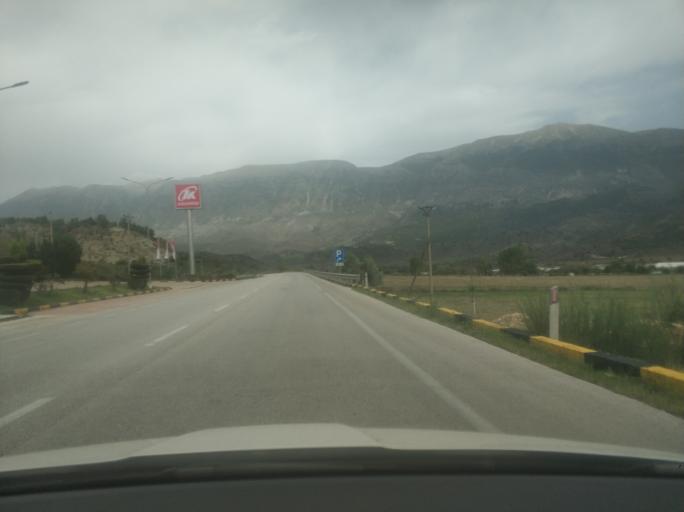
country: AL
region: Gjirokaster
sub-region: Rrethi i Gjirokastres
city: Picar
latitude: 40.1878
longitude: 20.0796
